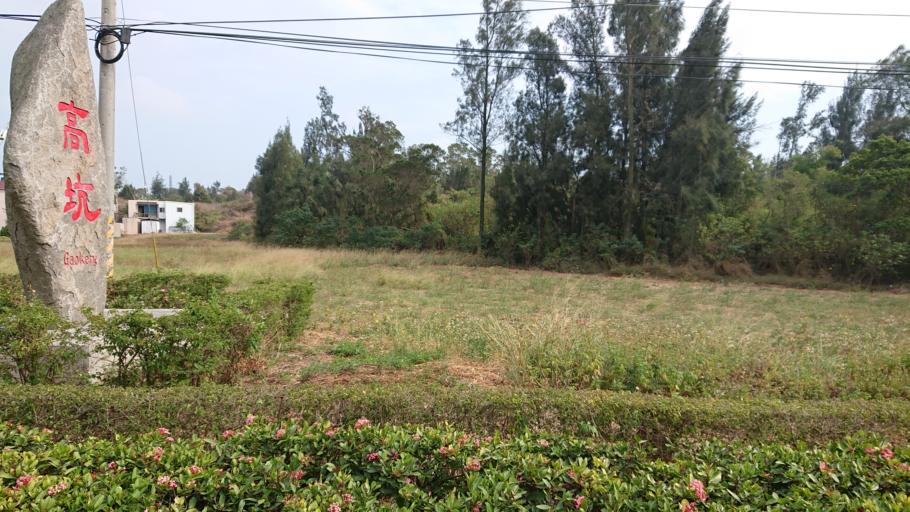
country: TW
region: Fukien
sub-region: Kinmen
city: Jincheng
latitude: 24.4665
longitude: 118.3886
